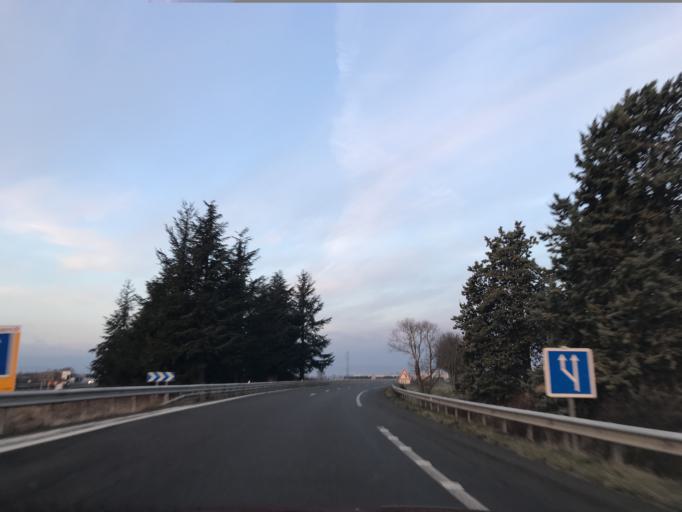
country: FR
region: Auvergne
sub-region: Departement du Puy-de-Dome
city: Pont-du-Chateau
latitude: 45.8289
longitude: 3.2310
